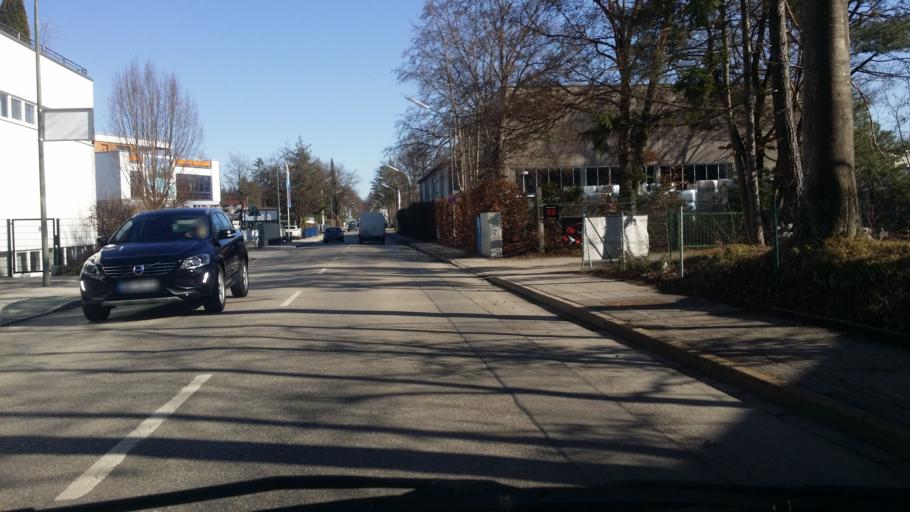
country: DE
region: Bavaria
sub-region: Upper Bavaria
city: Geretsried
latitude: 47.8552
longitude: 11.4905
